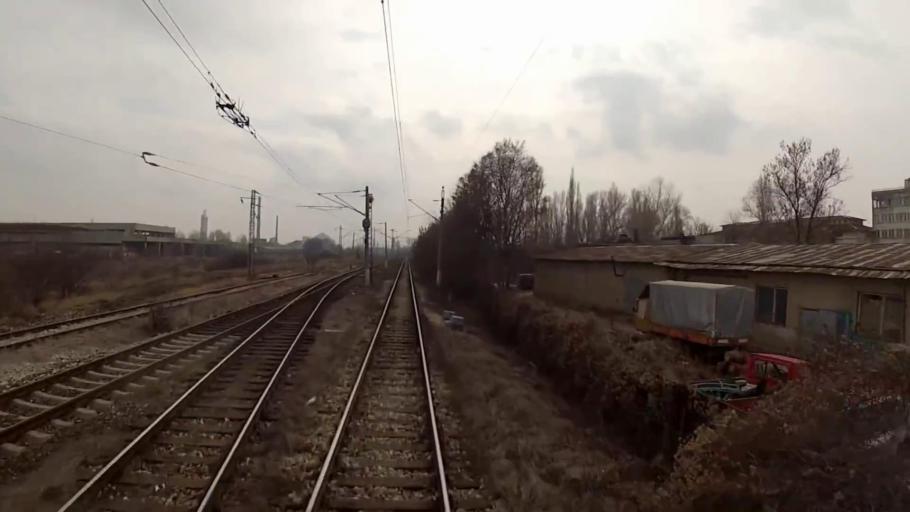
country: BG
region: Sofia-Capital
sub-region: Stolichna Obshtina
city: Sofia
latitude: 42.6616
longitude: 23.4269
